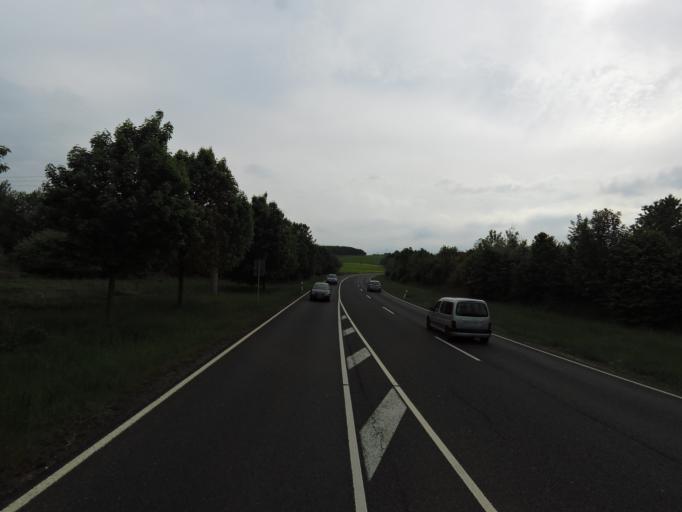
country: DE
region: Rheinland-Pfalz
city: Waldesch
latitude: 50.2783
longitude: 7.5499
